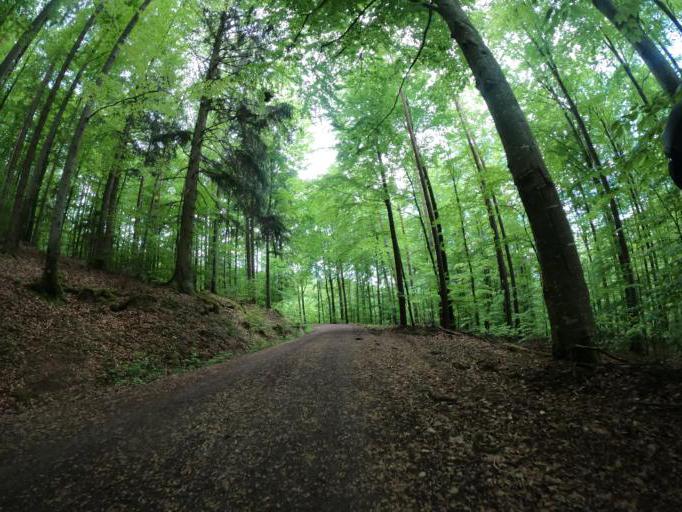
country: DE
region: Baden-Wuerttemberg
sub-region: Regierungsbezirk Stuttgart
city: Waldenbuch
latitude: 48.5997
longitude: 9.1391
